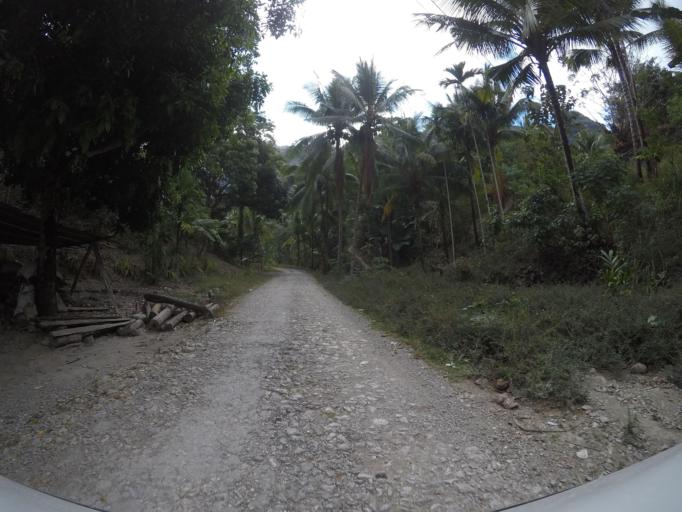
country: TL
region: Baucau
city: Baucau
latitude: -8.6210
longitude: 126.6571
